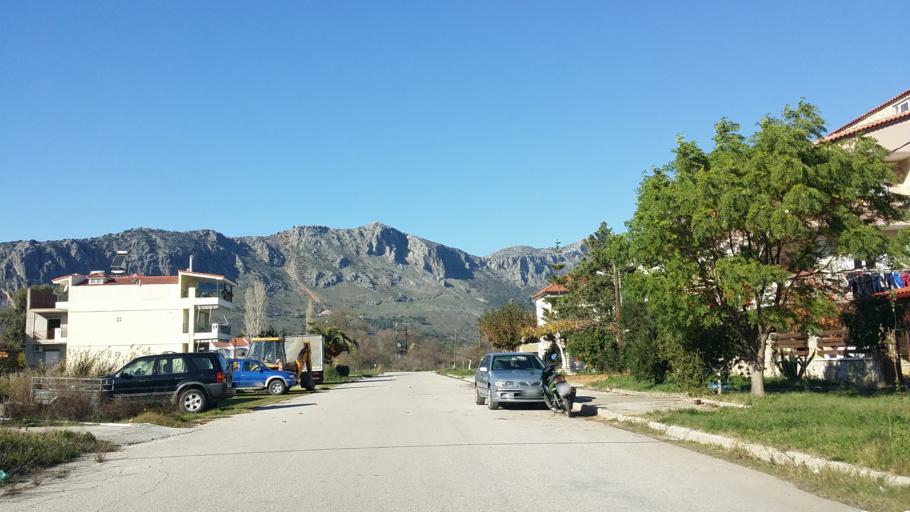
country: GR
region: West Greece
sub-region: Nomos Aitolias kai Akarnanias
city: Kandila
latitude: 38.6715
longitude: 20.9489
